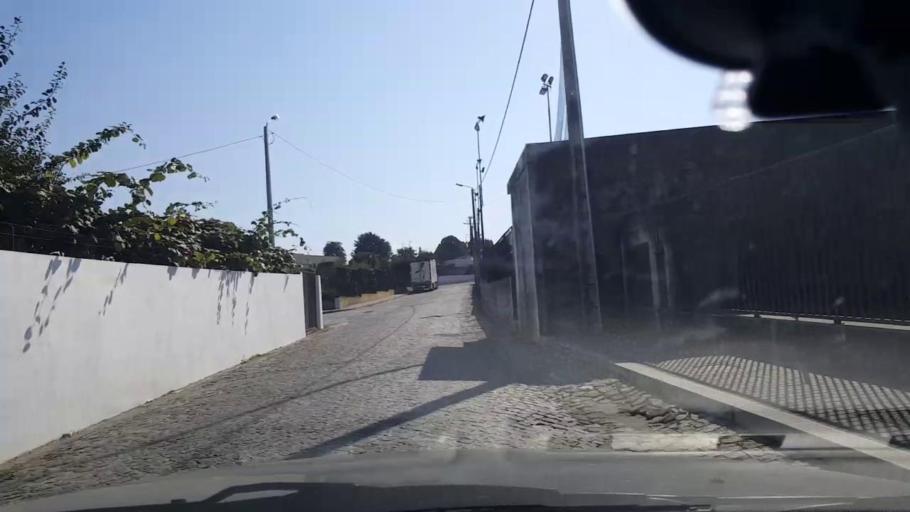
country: PT
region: Porto
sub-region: Vila do Conde
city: Arvore
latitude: 41.3810
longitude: -8.6818
